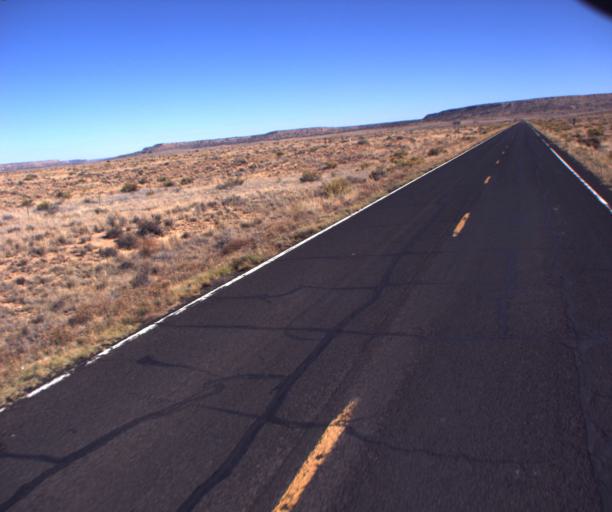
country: US
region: Arizona
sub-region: Navajo County
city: First Mesa
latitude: 35.8407
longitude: -110.3437
